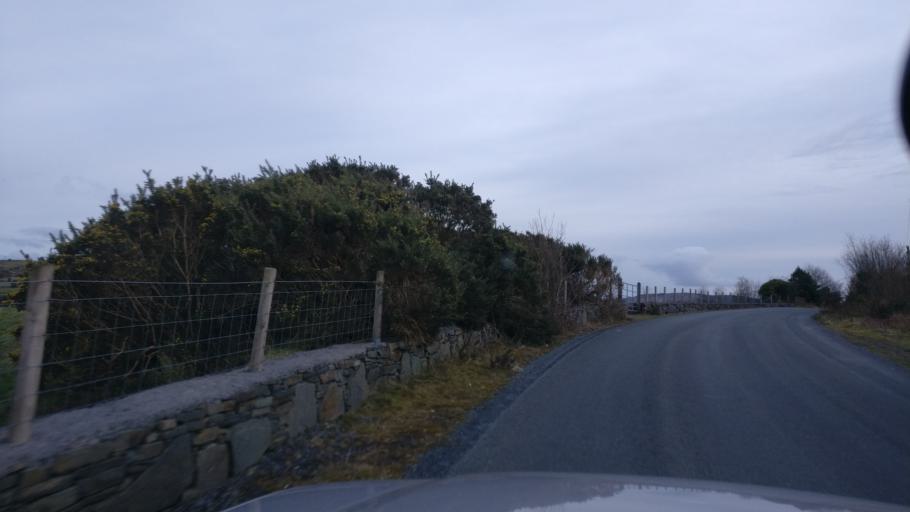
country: IE
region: Connaught
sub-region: County Galway
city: Oughterard
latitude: 53.5258
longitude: -9.4614
